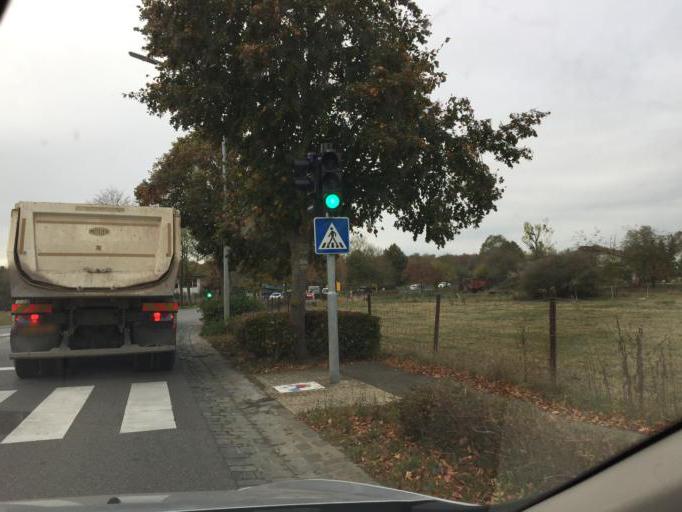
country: LU
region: Luxembourg
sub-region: Canton de Capellen
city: Kehlen
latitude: 49.6671
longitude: 6.0288
